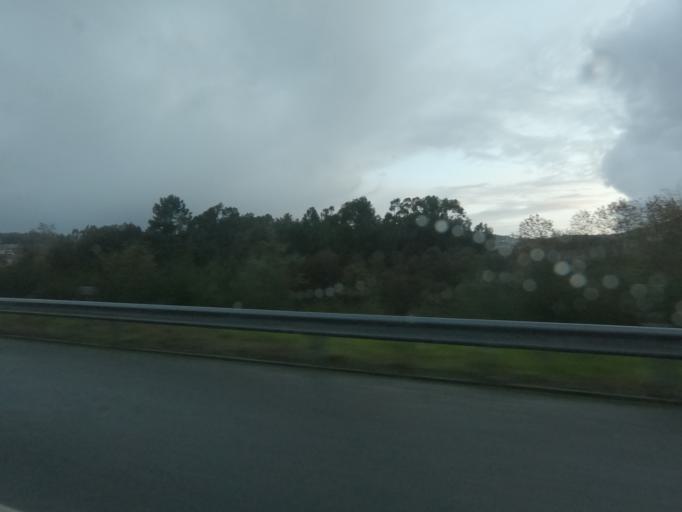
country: PT
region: Braga
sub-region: Braga
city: Oliveira
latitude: 41.5326
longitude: -8.4895
